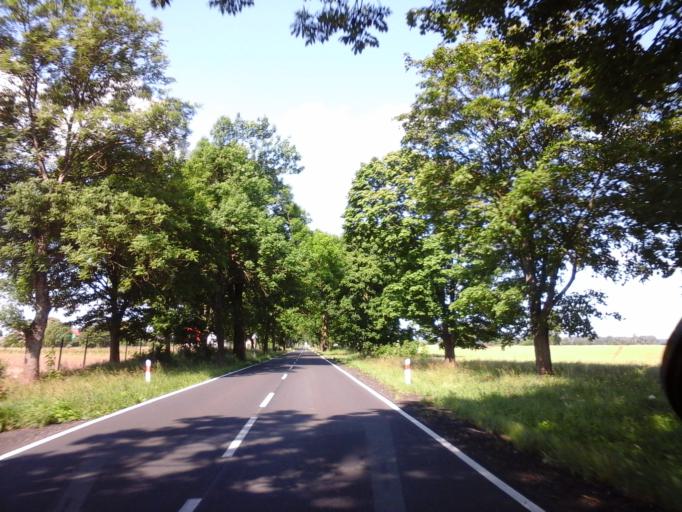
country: PL
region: West Pomeranian Voivodeship
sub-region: Powiat choszczenski
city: Recz
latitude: 53.1893
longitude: 15.5920
